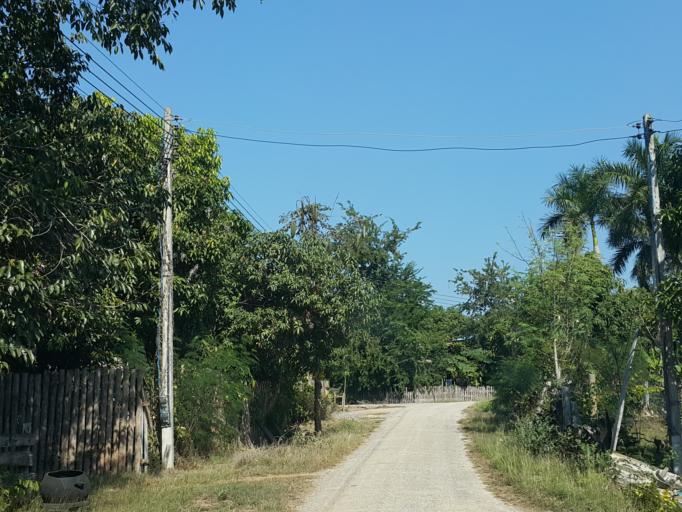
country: TH
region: Sukhothai
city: Thung Saliam
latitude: 17.3457
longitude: 99.4361
